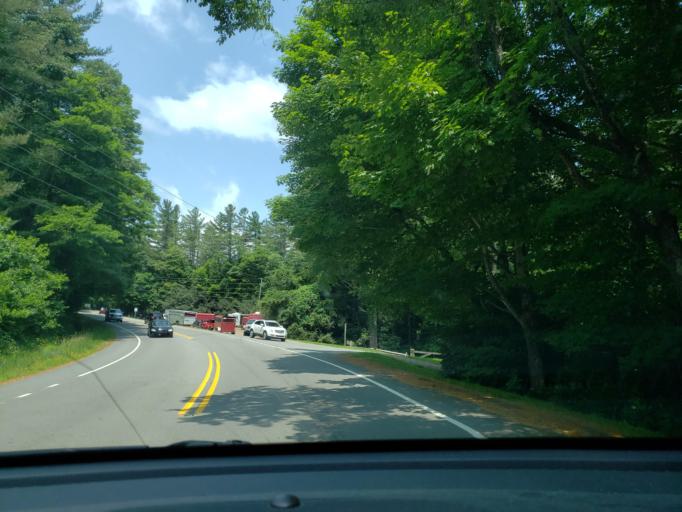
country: US
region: North Carolina
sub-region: Watauga County
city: Blowing Rock
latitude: 36.1386
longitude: -81.6860
